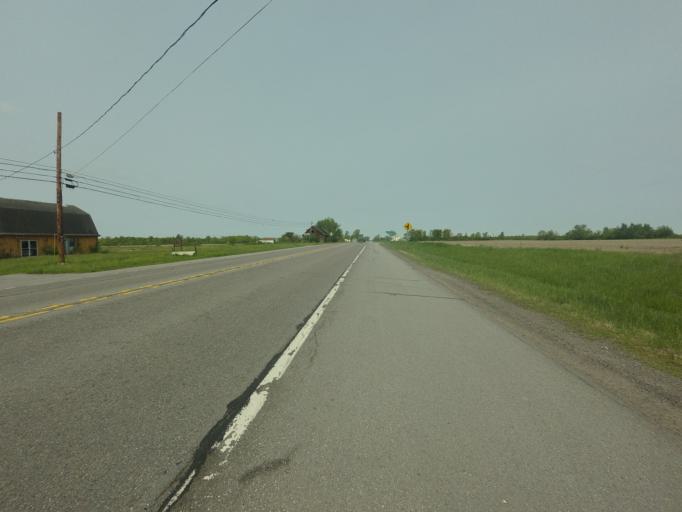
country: US
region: New York
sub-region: Jefferson County
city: Dexter
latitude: 44.0305
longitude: -76.0510
